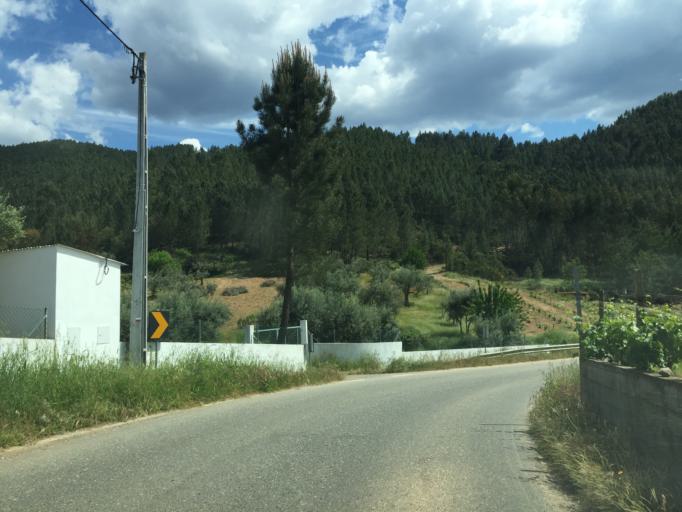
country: PT
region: Coimbra
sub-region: Pampilhosa da Serra
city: Pampilhosa da Serra
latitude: 40.0606
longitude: -7.7978
